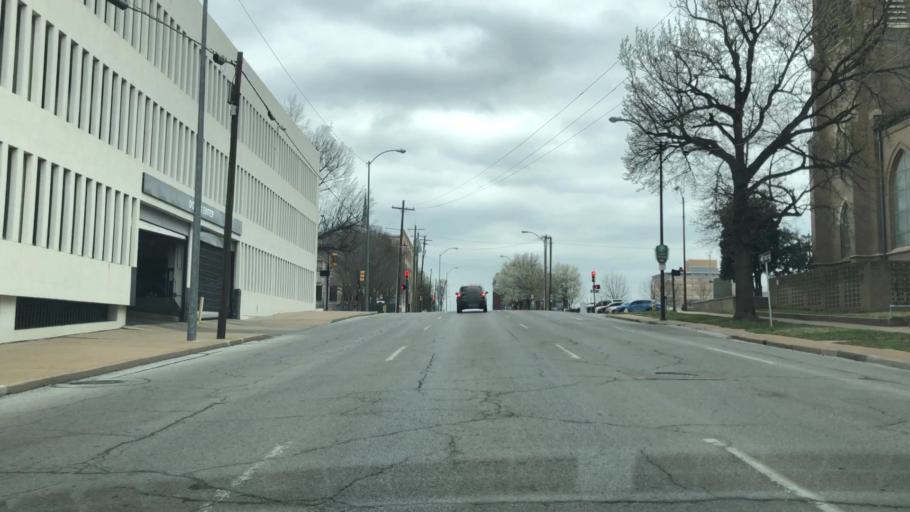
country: US
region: Oklahoma
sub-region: Tulsa County
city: Tulsa
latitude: 36.1479
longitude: -95.9905
